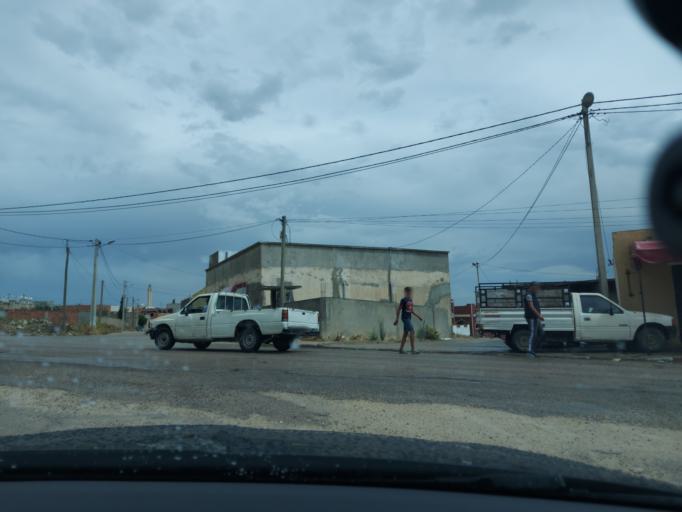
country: TN
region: Silyanah
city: Maktar
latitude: 35.8523
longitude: 9.2153
